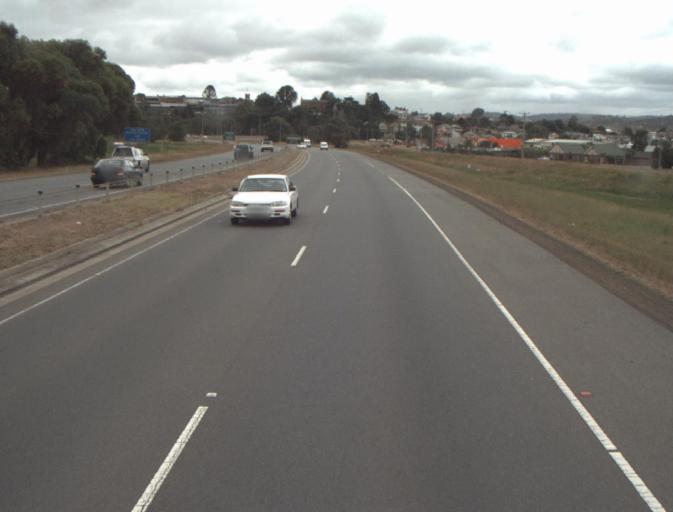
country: AU
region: Tasmania
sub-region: Launceston
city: Newnham
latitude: -41.4160
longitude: 147.1301
